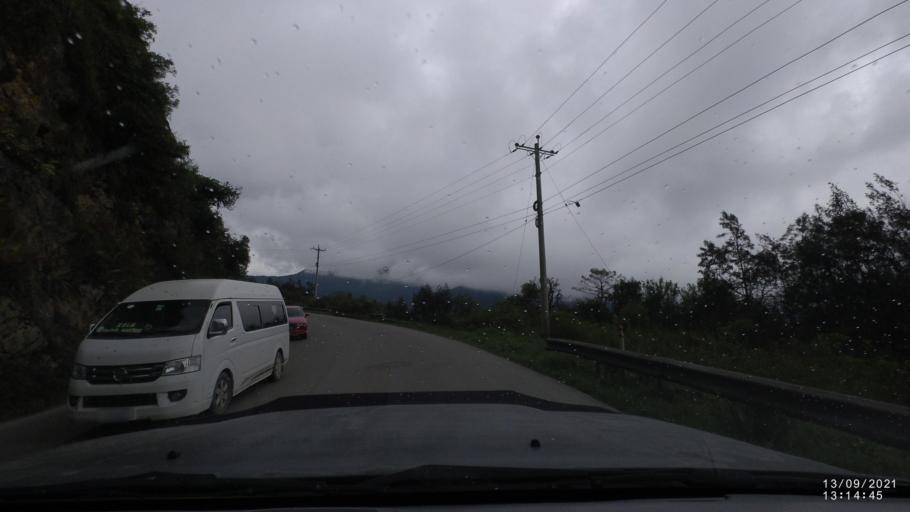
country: BO
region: Cochabamba
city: Colomi
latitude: -17.1950
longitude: -65.8518
